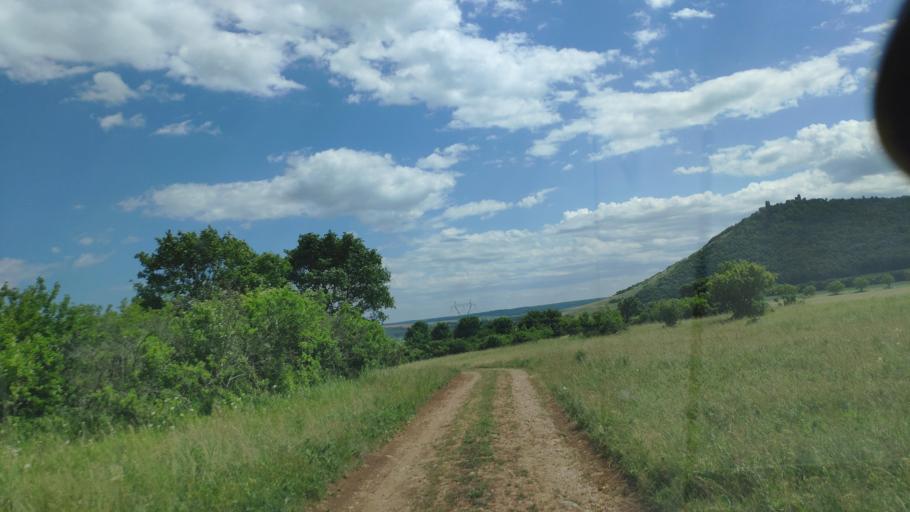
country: SK
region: Kosicky
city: Medzev
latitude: 48.6238
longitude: 20.8757
